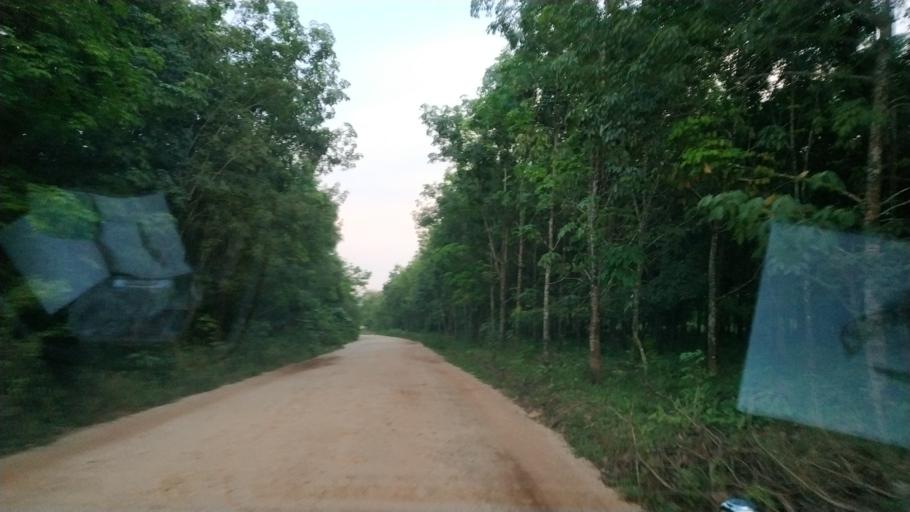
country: MM
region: Mon
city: Kyaikto
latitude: 17.4191
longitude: 97.0527
